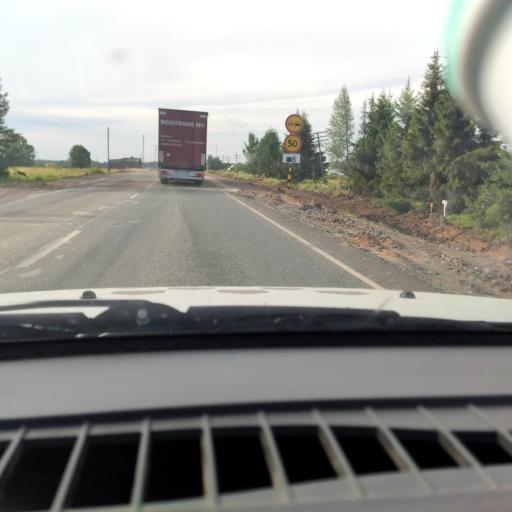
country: RU
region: Kirov
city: Kostino
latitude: 58.8326
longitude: 53.3068
